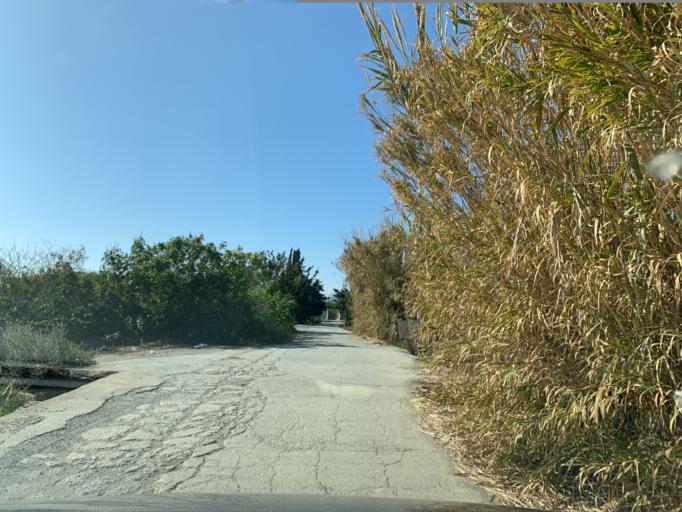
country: ES
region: Andalusia
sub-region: Provincia de Granada
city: El Varadero
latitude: 36.7258
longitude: -3.5559
